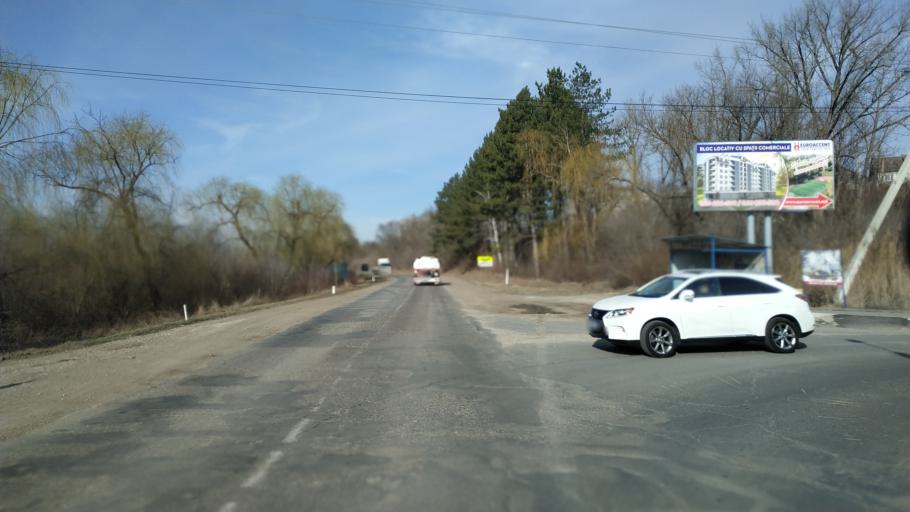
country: MD
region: Laloveni
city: Ialoveni
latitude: 46.9520
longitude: 28.7635
